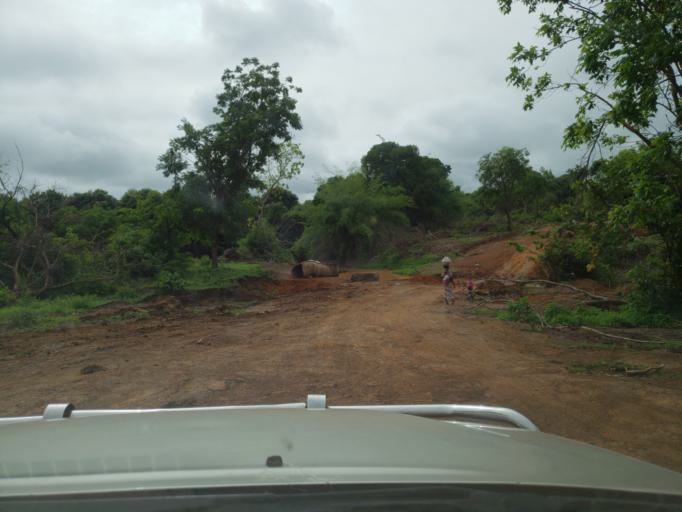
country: ML
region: Koulikoro
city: Kangaba
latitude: 12.0248
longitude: -8.7158
